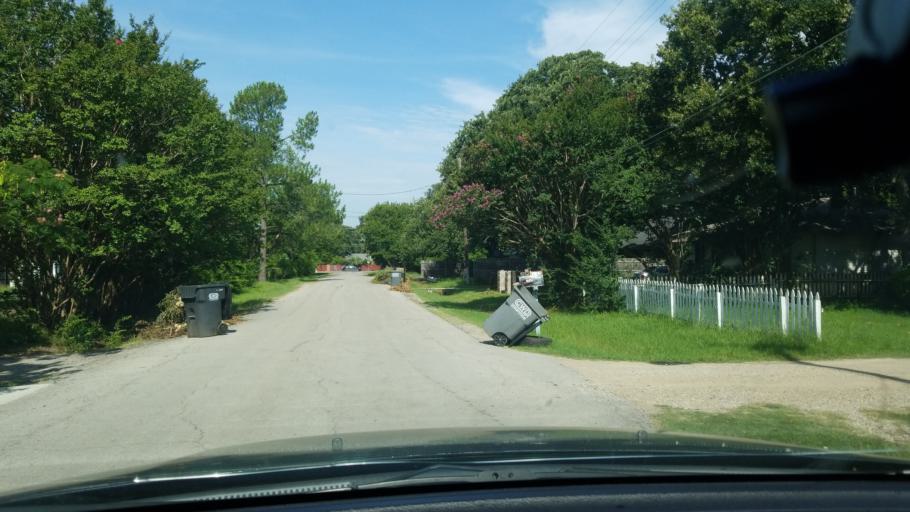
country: US
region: Texas
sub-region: Dallas County
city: Balch Springs
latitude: 32.7276
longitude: -96.6373
